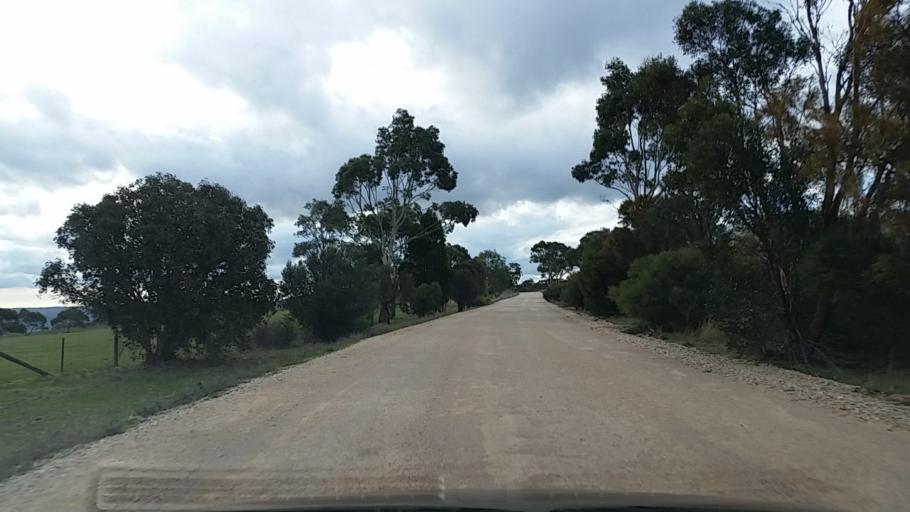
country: AU
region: South Australia
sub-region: Mount Barker
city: Callington
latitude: -34.9944
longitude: 139.0572
